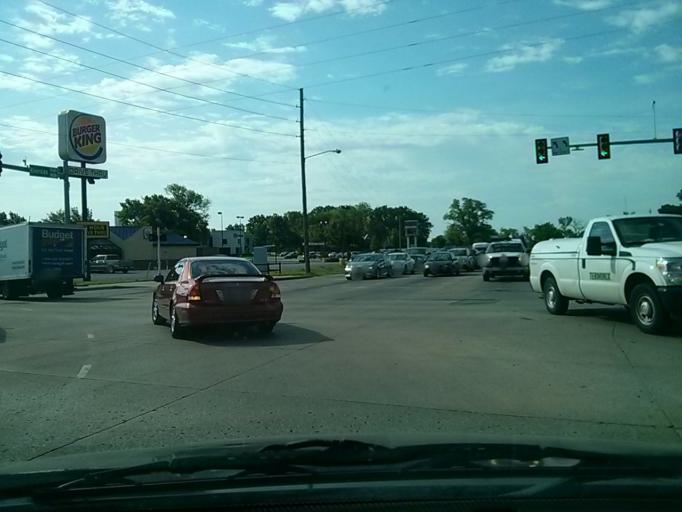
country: US
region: Oklahoma
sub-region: Tulsa County
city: Jenks
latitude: 36.0607
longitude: -95.9758
